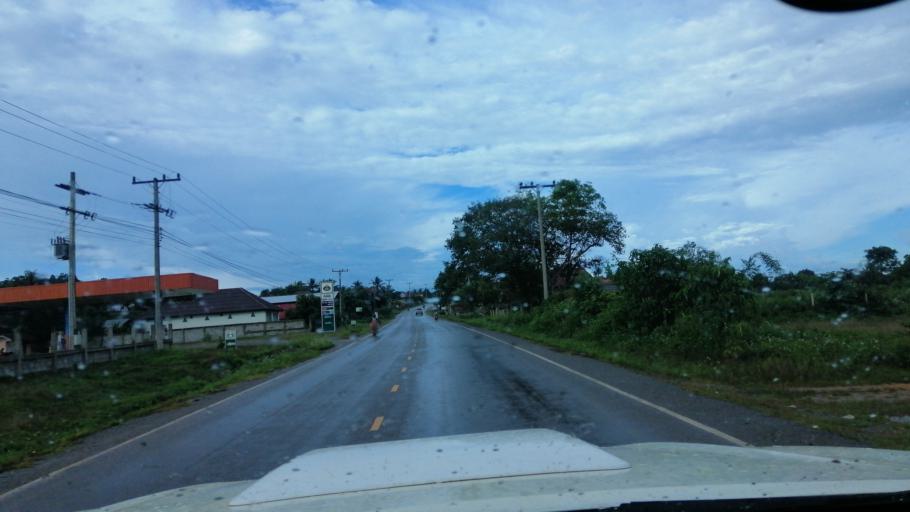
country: TH
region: Nan
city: Thung Chang
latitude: 19.6347
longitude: 100.8132
